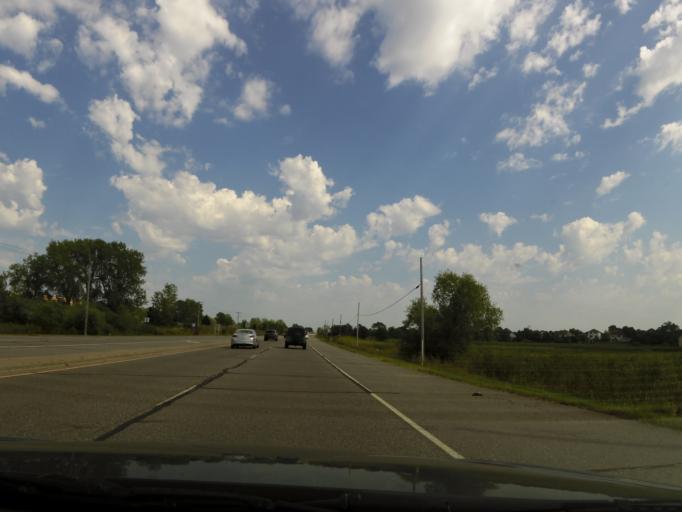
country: US
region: Minnesota
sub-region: Washington County
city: Oakdale
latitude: 44.9633
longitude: -92.9481
